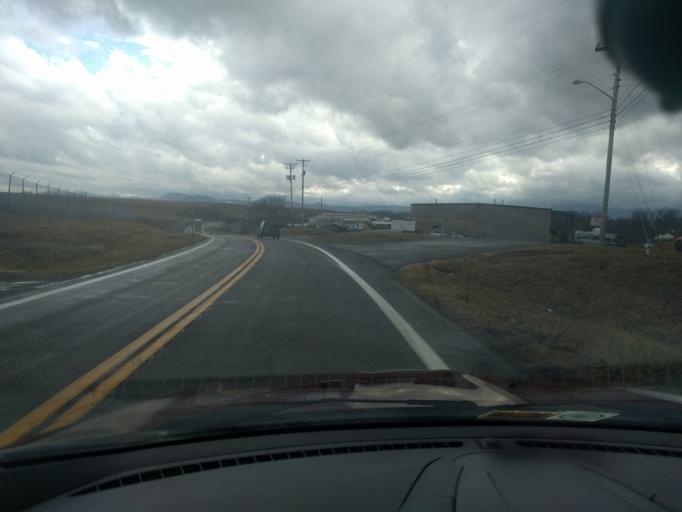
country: US
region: Virginia
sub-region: Roanoke County
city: Hollins
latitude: 37.3270
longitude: -79.9861
